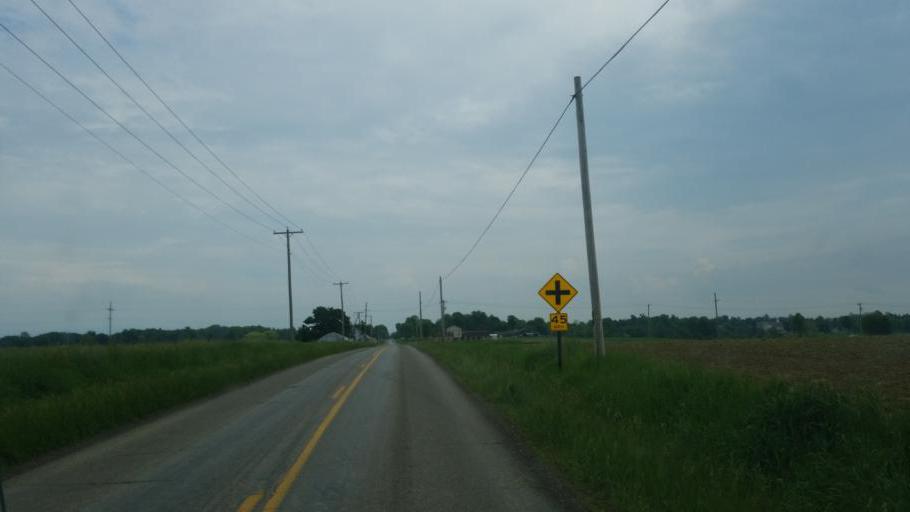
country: US
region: Ohio
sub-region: Wayne County
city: Dalton
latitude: 40.7558
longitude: -81.7570
